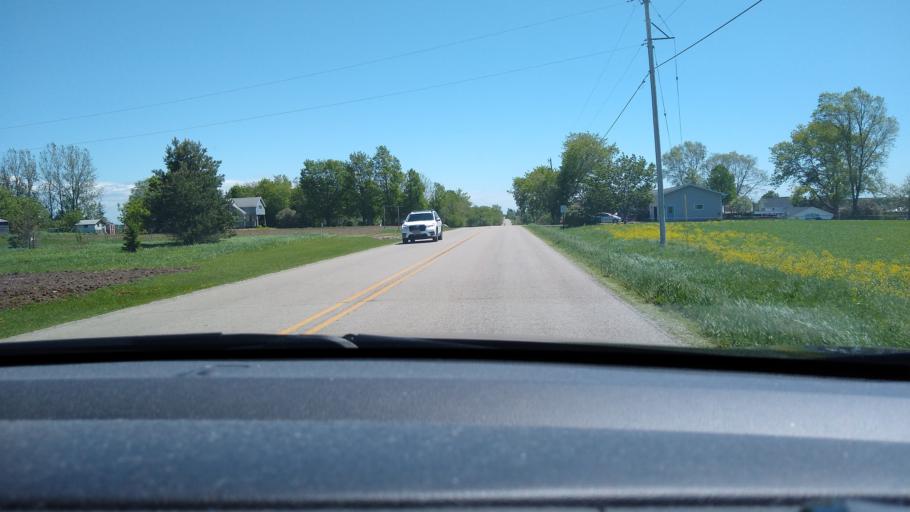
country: US
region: Michigan
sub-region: Delta County
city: Escanaba
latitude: 45.8261
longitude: -87.1610
